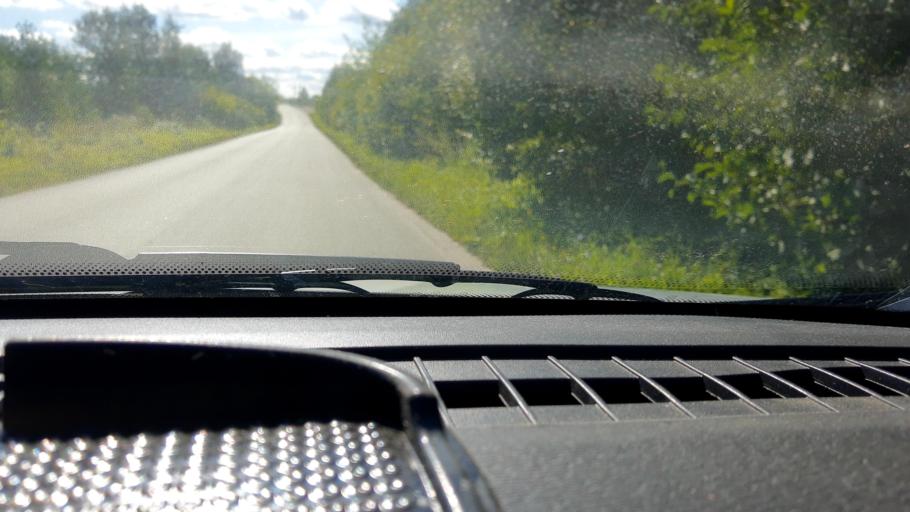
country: RU
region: Nizjnij Novgorod
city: Lukino
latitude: 56.4222
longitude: 43.6526
